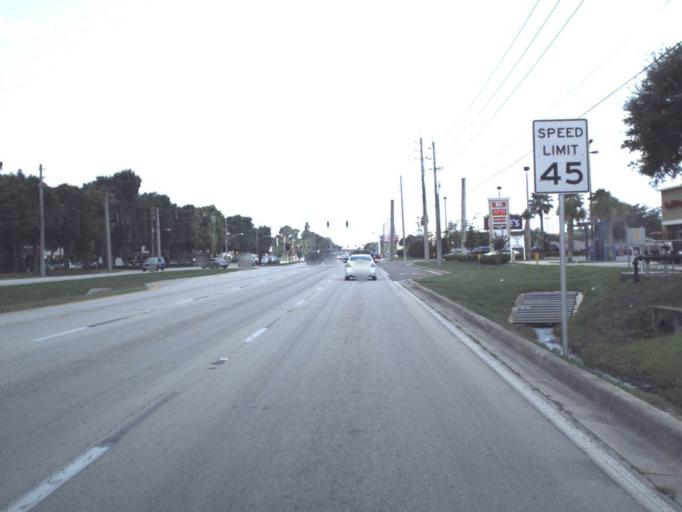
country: US
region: Florida
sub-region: Saint Johns County
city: Fruit Cove
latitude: 30.2247
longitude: -81.5881
